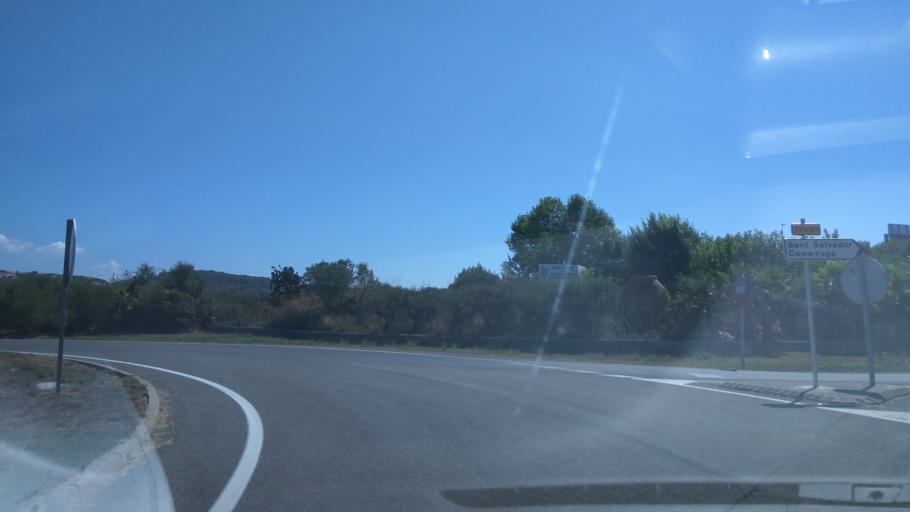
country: ES
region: Catalonia
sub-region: Provincia de Tarragona
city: El Vendrell
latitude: 41.1956
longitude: 1.5377
